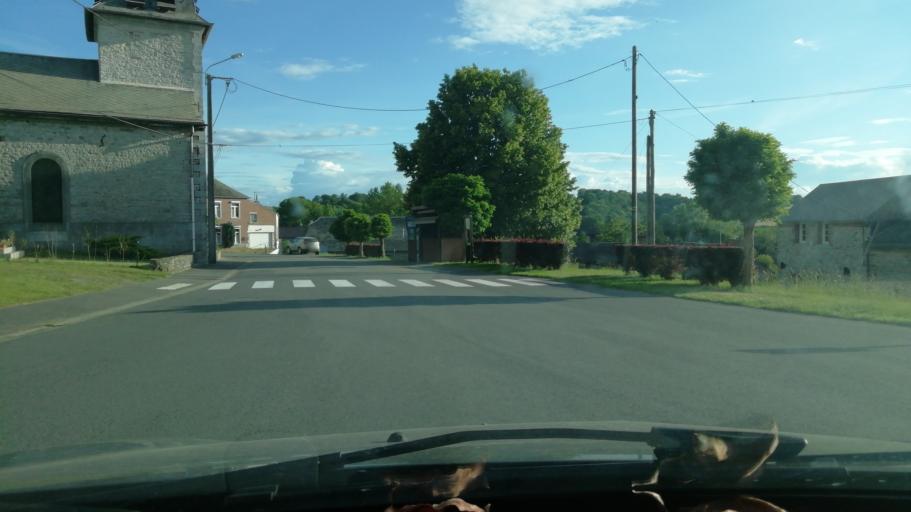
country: BE
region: Wallonia
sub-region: Province du Hainaut
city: Merbes-le-Chateau
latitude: 50.2639
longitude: 4.1819
